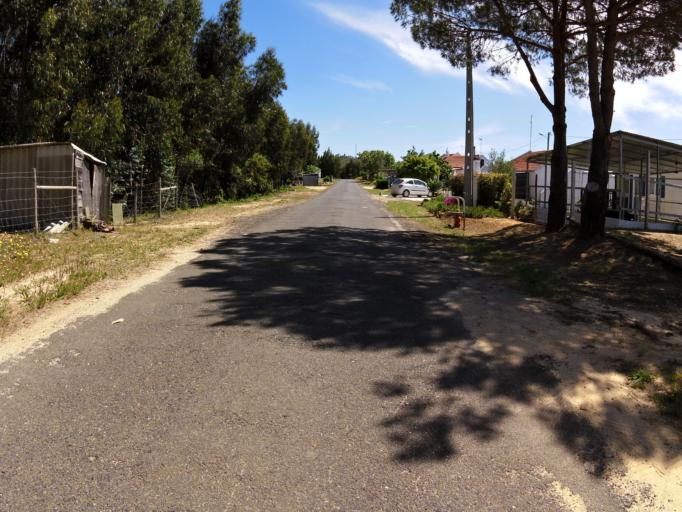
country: PT
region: Setubal
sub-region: Santiago do Cacem
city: Santiago do Cacem
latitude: 37.9447
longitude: -8.7304
